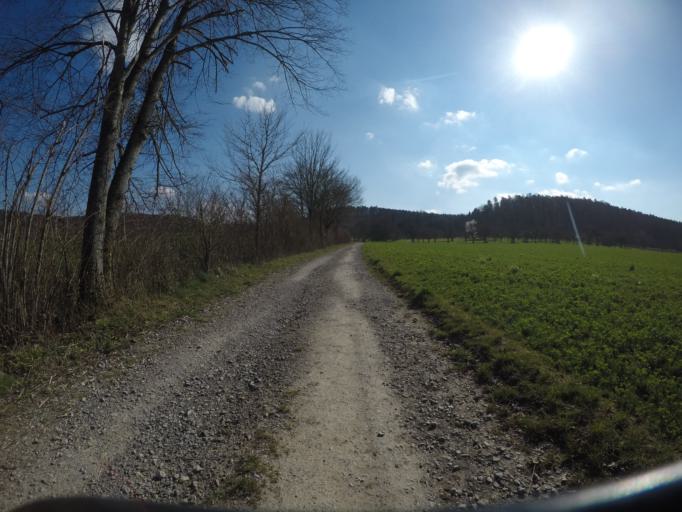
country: DE
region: Baden-Wuerttemberg
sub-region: Tuebingen Region
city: Dusslingen
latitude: 48.4866
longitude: 9.0273
